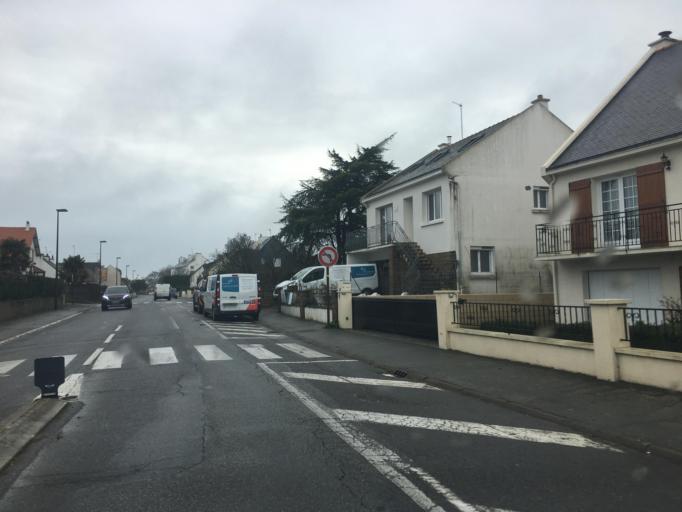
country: FR
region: Pays de la Loire
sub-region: Departement de la Loire-Atlantique
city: Guerande
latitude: 47.3325
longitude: -2.4220
